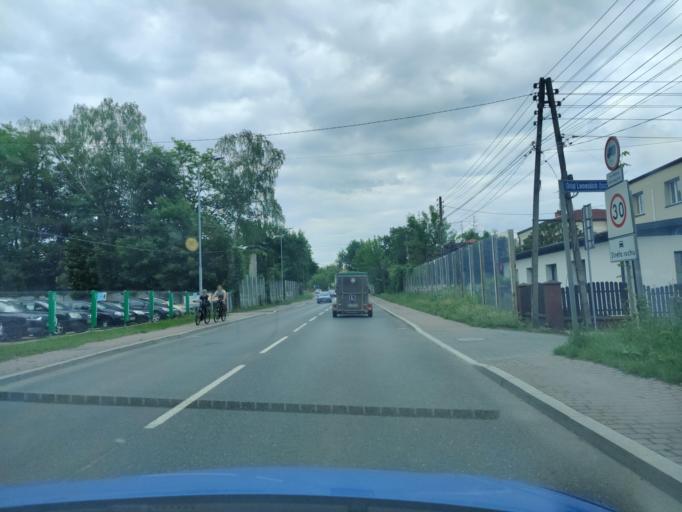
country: PL
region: Silesian Voivodeship
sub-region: Myslowice
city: Myslowice
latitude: 50.2341
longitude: 19.1620
